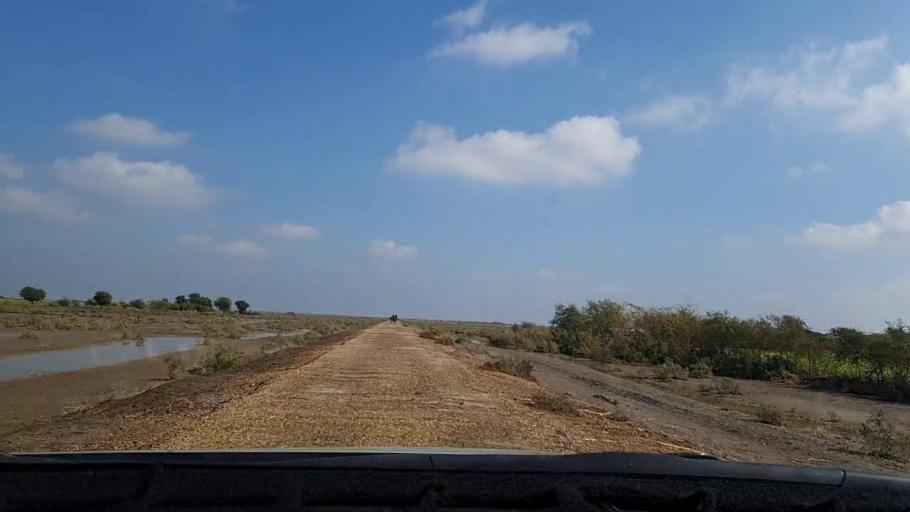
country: PK
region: Sindh
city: Pithoro
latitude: 25.7369
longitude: 69.2726
